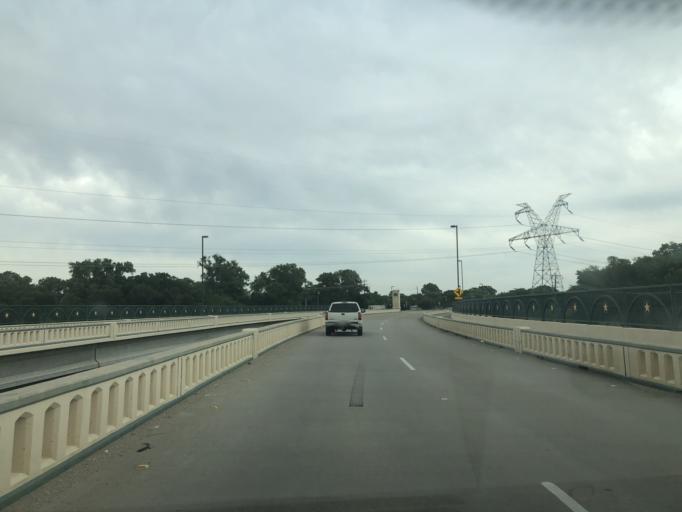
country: US
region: Texas
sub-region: Dallas County
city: Grand Prairie
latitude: 32.7819
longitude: -96.9767
